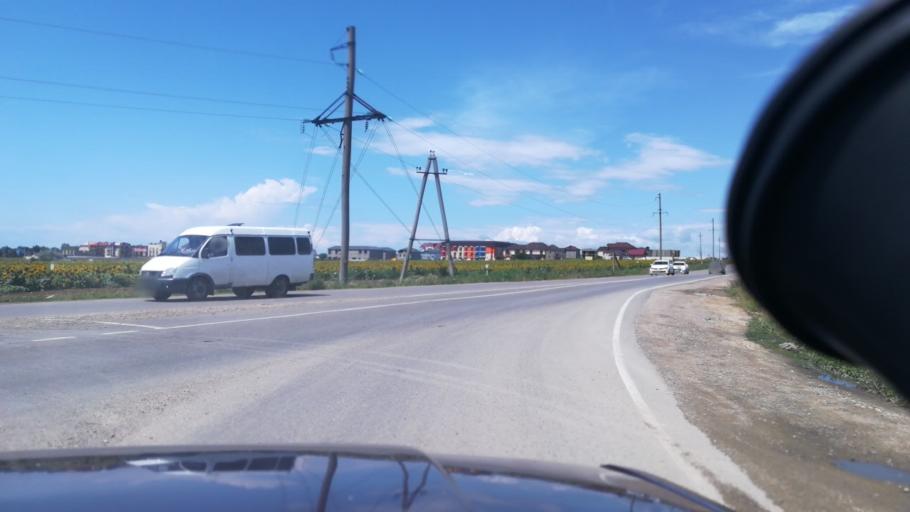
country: RU
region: Krasnodarskiy
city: Tsibanobalka
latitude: 44.9595
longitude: 37.3060
